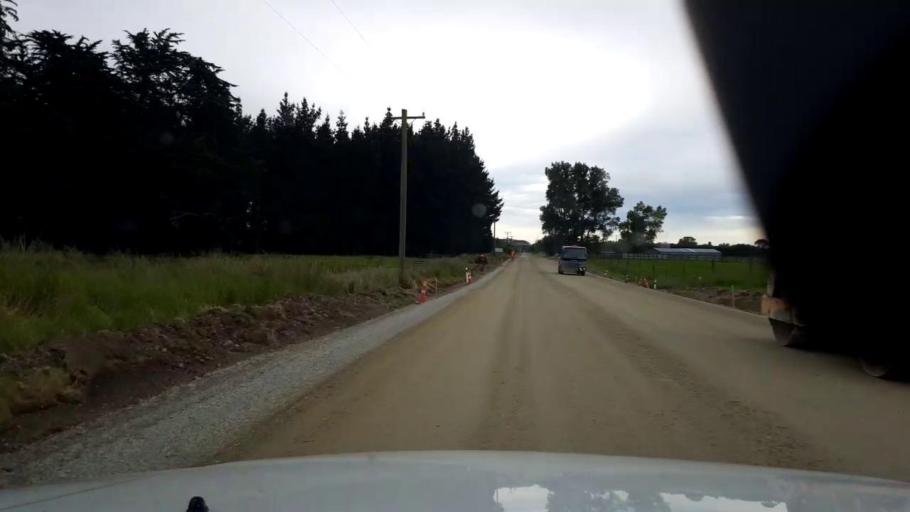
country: NZ
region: Canterbury
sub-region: Timaru District
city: Pleasant Point
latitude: -44.2764
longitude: 171.2508
